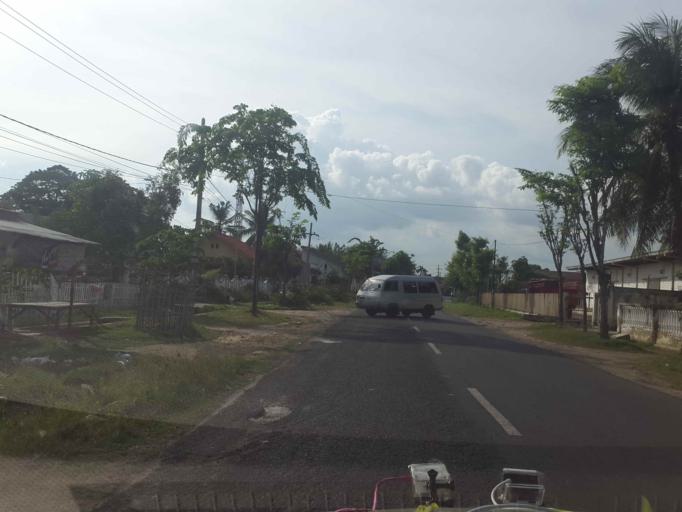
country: ID
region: East Java
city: Penatu
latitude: -7.0387
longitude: 113.8993
